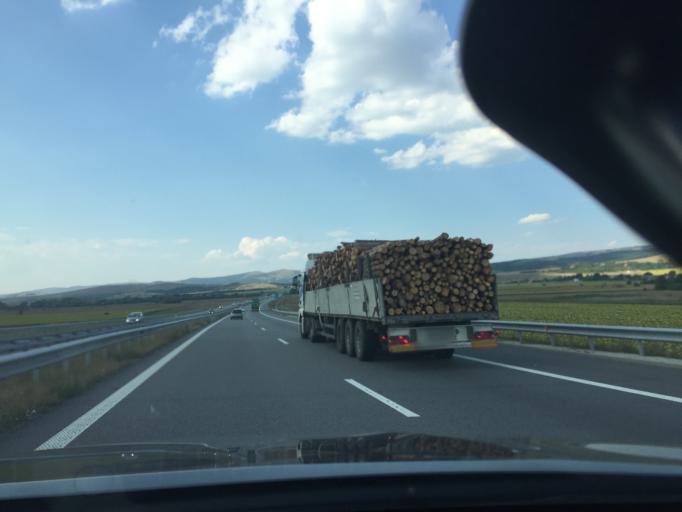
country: BG
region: Kyustendil
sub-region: Obshtina Bobovdol
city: Bobovdol
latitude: 42.4369
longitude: 23.1128
